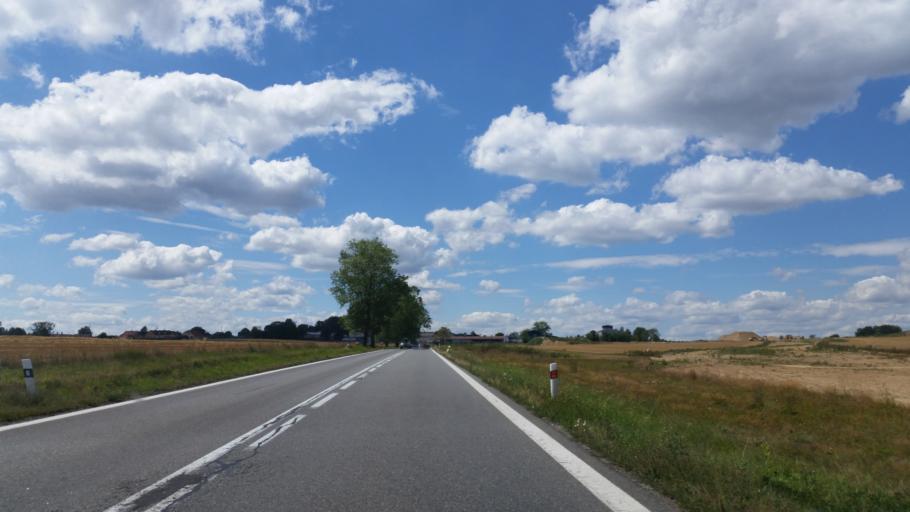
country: CZ
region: Vysocina
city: Pacov
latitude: 49.4249
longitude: 15.0279
